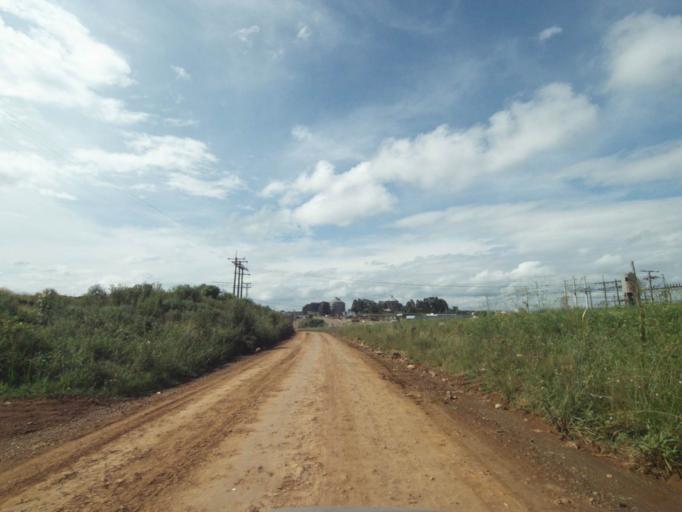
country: BR
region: Rio Grande do Sul
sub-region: Lagoa Vermelha
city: Lagoa Vermelha
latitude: -28.2168
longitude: -51.5101
